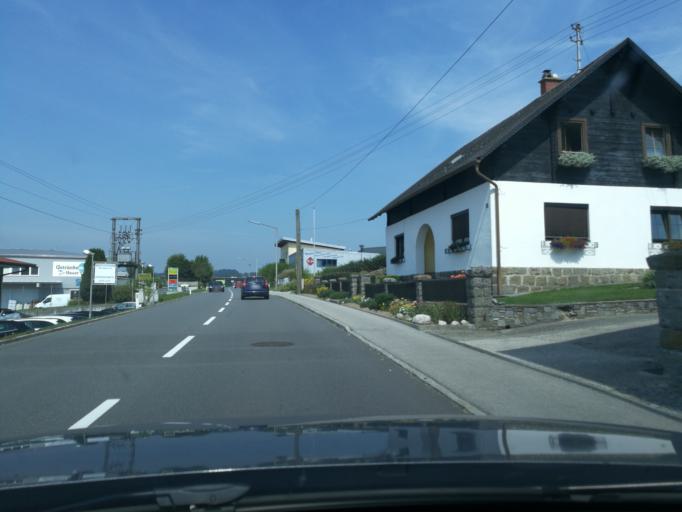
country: AT
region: Upper Austria
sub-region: Politischer Bezirk Grieskirchen
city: Grieskirchen
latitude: 48.3302
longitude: 13.7720
